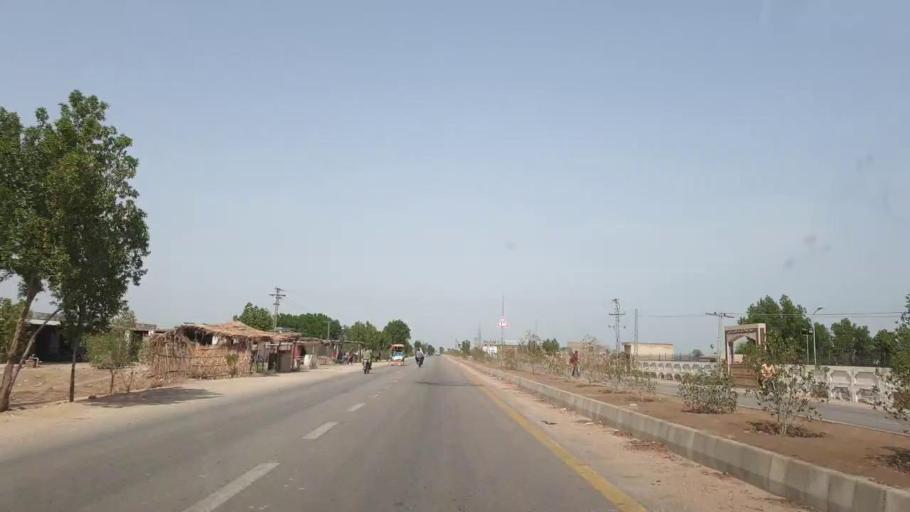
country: PK
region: Sindh
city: Nawabshah
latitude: 26.2222
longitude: 68.3469
